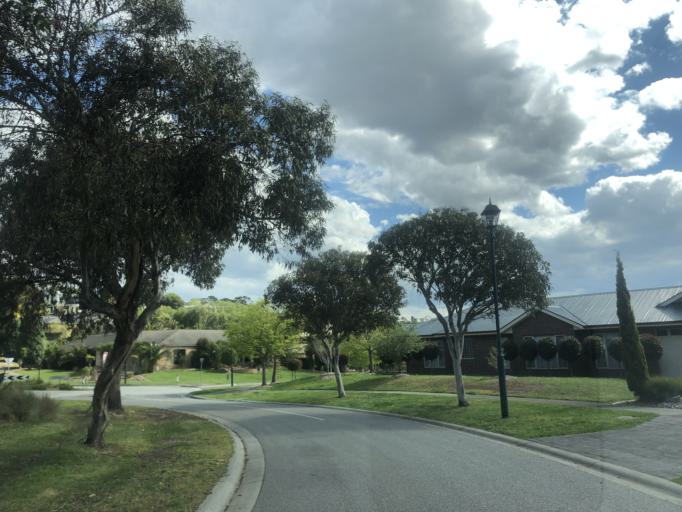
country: AU
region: Victoria
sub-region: Casey
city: Endeavour Hills
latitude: -37.9568
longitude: 145.2783
